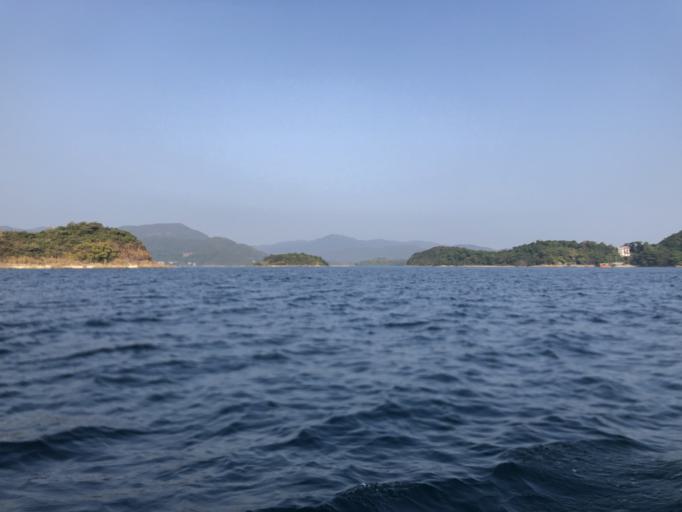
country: HK
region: Sai Kung
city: Sai Kung
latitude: 22.3715
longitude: 114.2839
